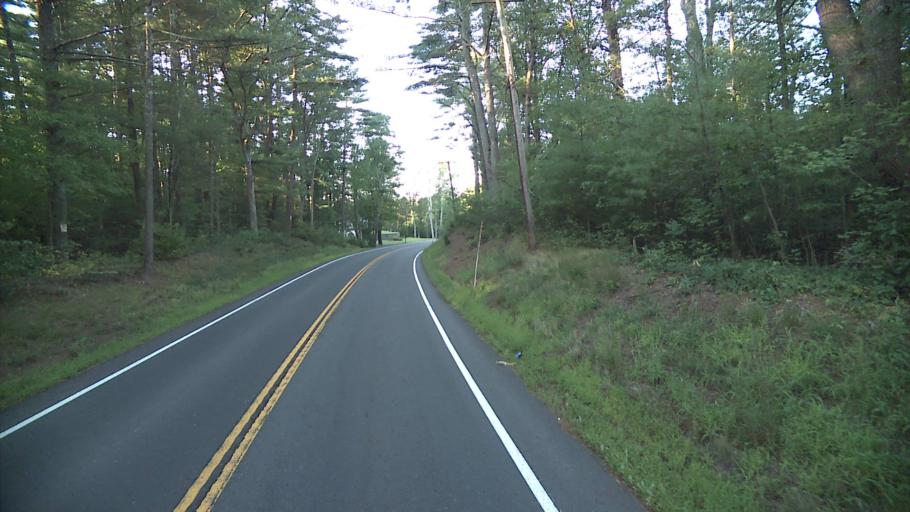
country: US
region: Connecticut
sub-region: Tolland County
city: Stafford
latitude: 42.0283
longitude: -72.3207
